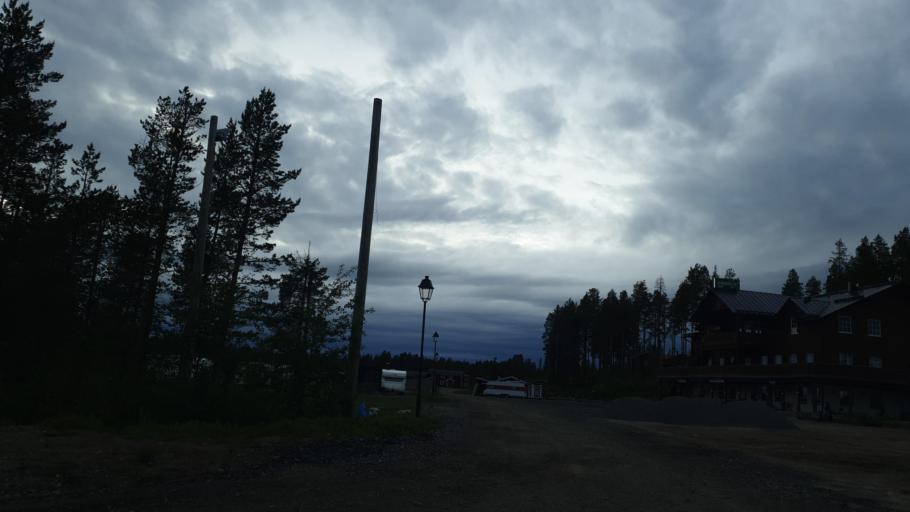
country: SE
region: Norrbotten
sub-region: Jokkmokks Kommun
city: Jokkmokk
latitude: 66.1546
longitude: 19.9898
